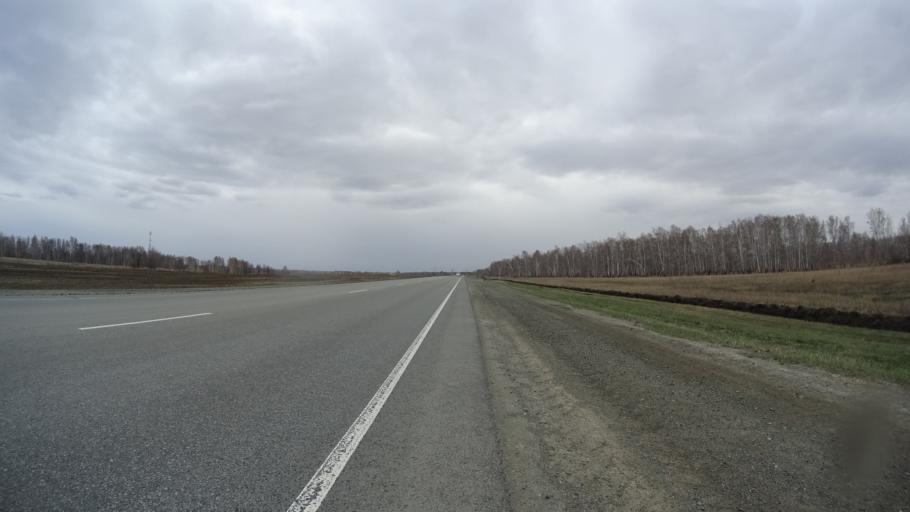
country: RU
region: Chelyabinsk
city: Krasnogorskiy
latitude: 54.6904
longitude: 61.2487
